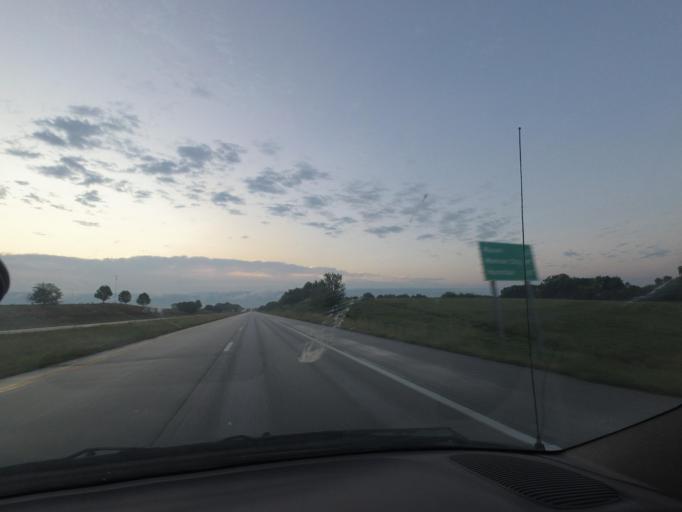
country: US
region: Missouri
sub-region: Macon County
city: Macon
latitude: 39.7591
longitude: -92.5494
